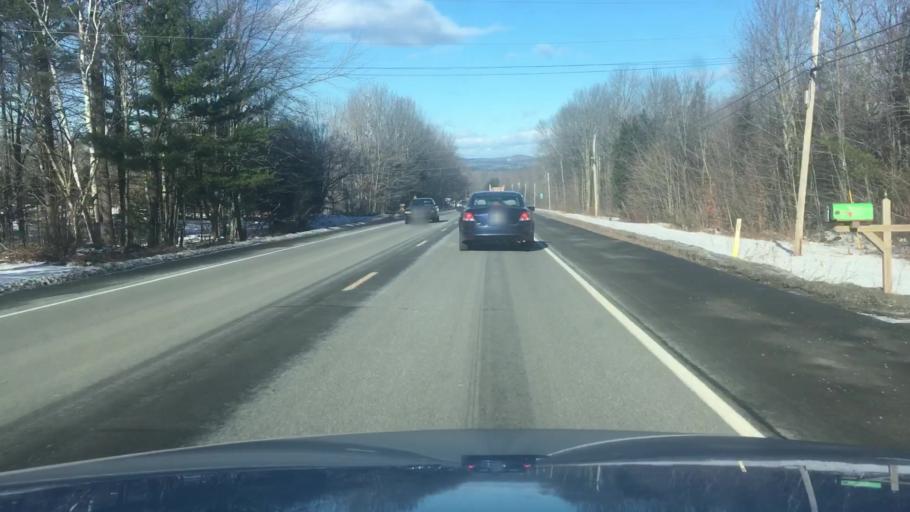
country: US
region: Maine
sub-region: Somerset County
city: Fairfield
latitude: 44.6291
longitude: -69.6771
